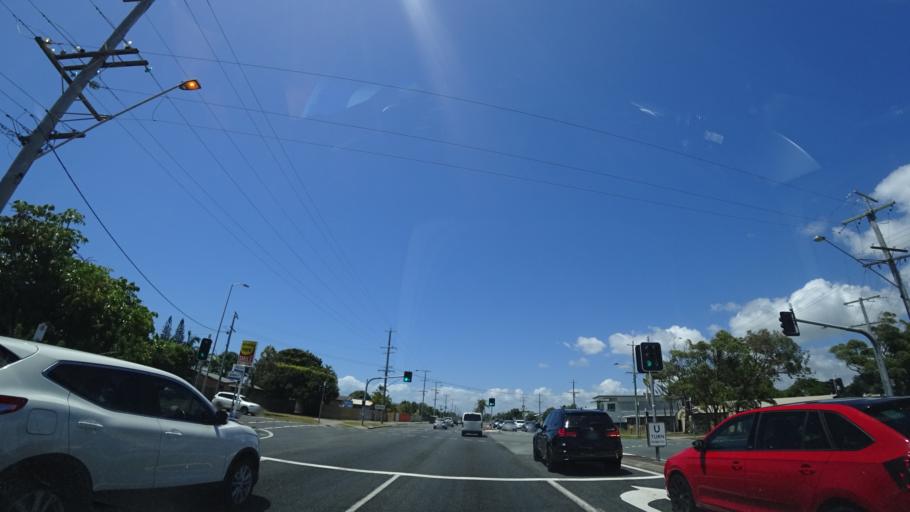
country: AU
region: Queensland
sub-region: Sunshine Coast
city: Mooloolaba
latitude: -26.7086
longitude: 153.1302
